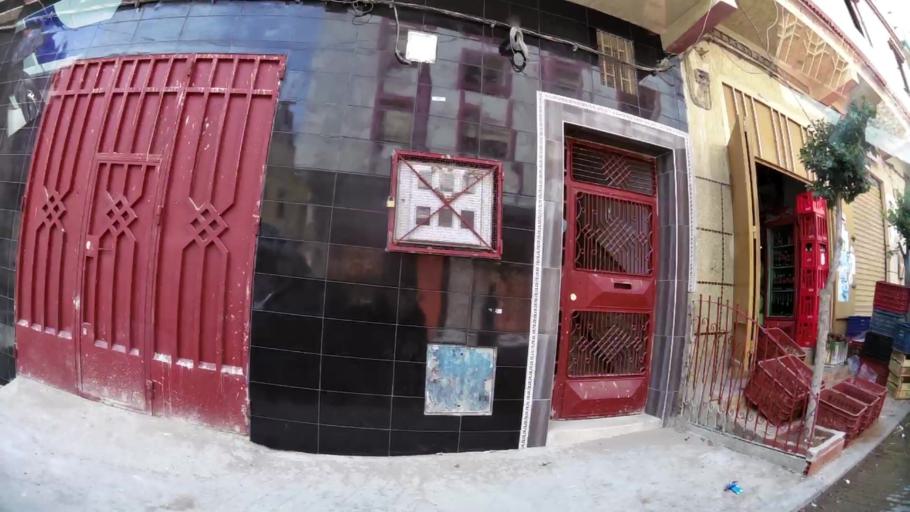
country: MA
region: Tanger-Tetouan
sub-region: Tanger-Assilah
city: Tangier
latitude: 35.7579
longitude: -5.8046
